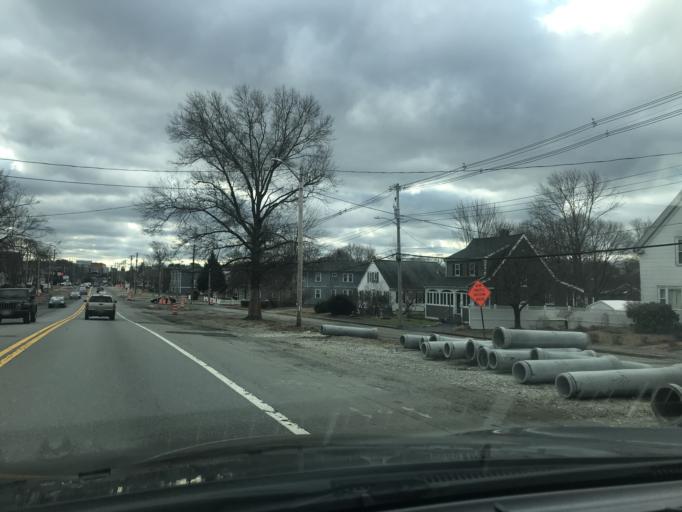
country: US
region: Massachusetts
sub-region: Norfolk County
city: Weymouth
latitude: 42.1850
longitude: -70.9555
